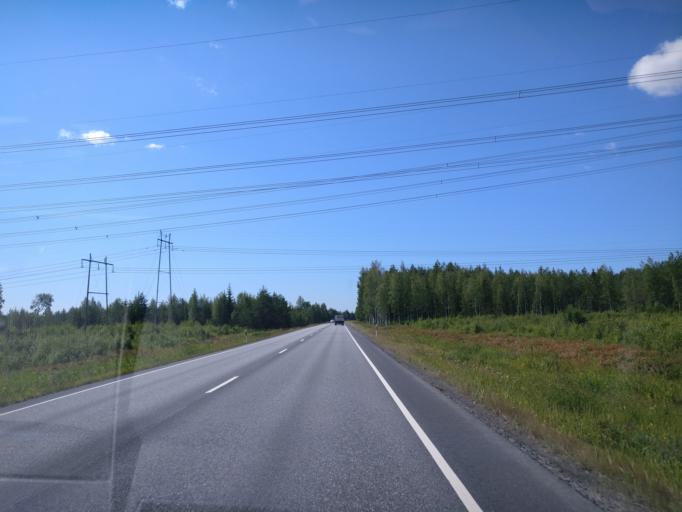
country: FI
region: Satakunta
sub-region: Pori
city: Kullaa
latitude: 61.4583
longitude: 22.0731
